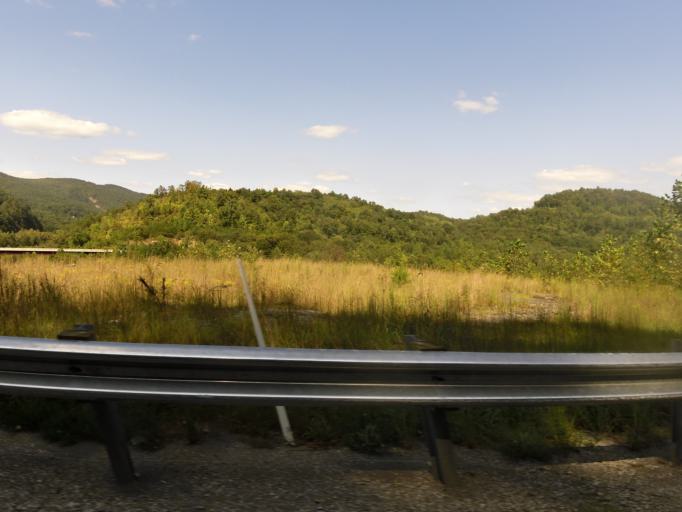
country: US
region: Kentucky
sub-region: Bell County
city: Pineville
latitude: 36.7411
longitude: -83.6099
